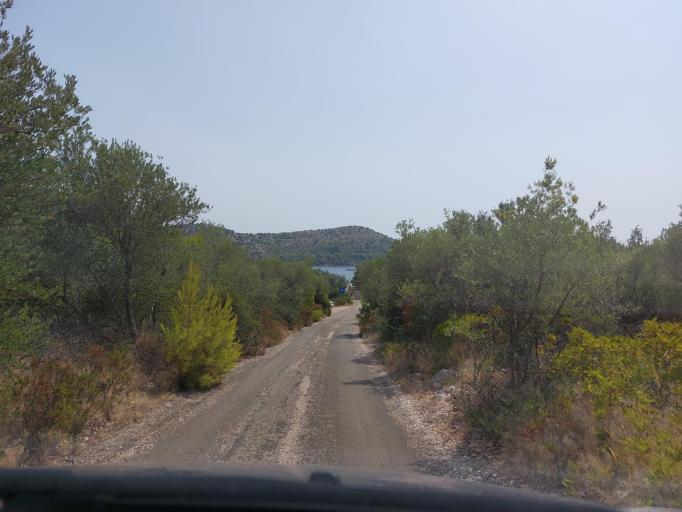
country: HR
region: Dubrovacko-Neretvanska
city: Smokvica
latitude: 42.7385
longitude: 16.8875
